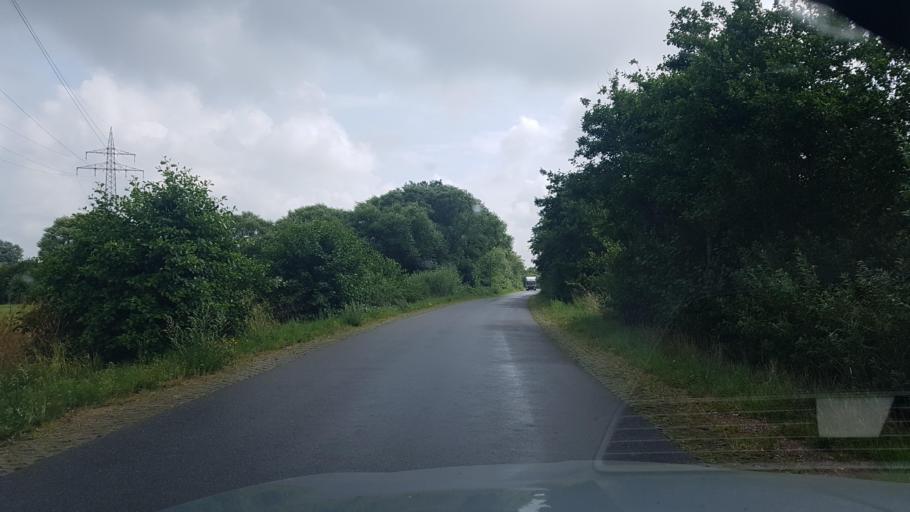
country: DE
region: Schleswig-Holstein
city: Tumlauer Koog
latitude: 54.3209
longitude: 8.6743
